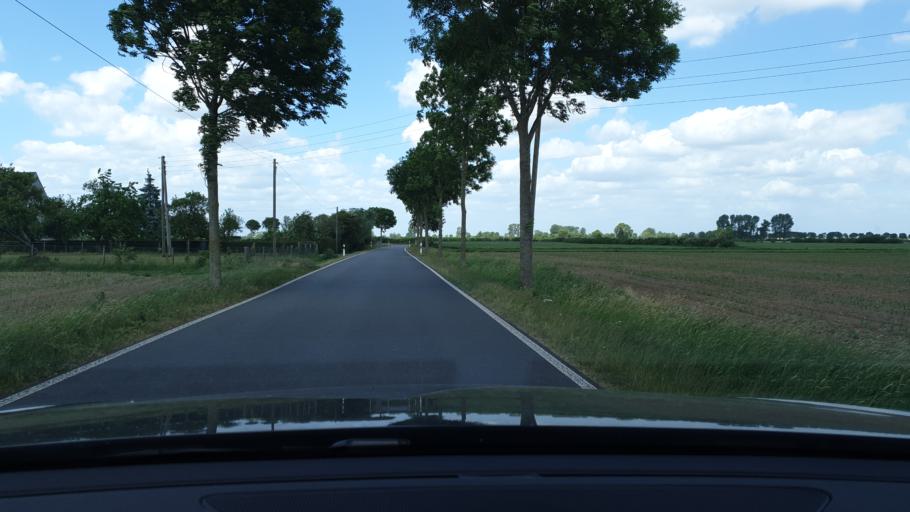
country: DE
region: North Rhine-Westphalia
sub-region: Regierungsbezirk Dusseldorf
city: Kranenburg
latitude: 51.8212
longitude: 6.0437
